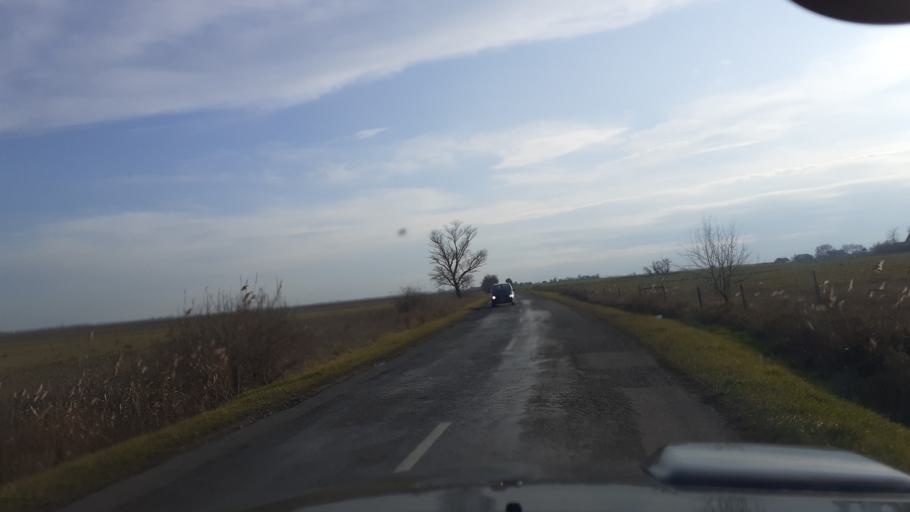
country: HU
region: Bacs-Kiskun
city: Kunszentmiklos
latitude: 47.0884
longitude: 19.0946
